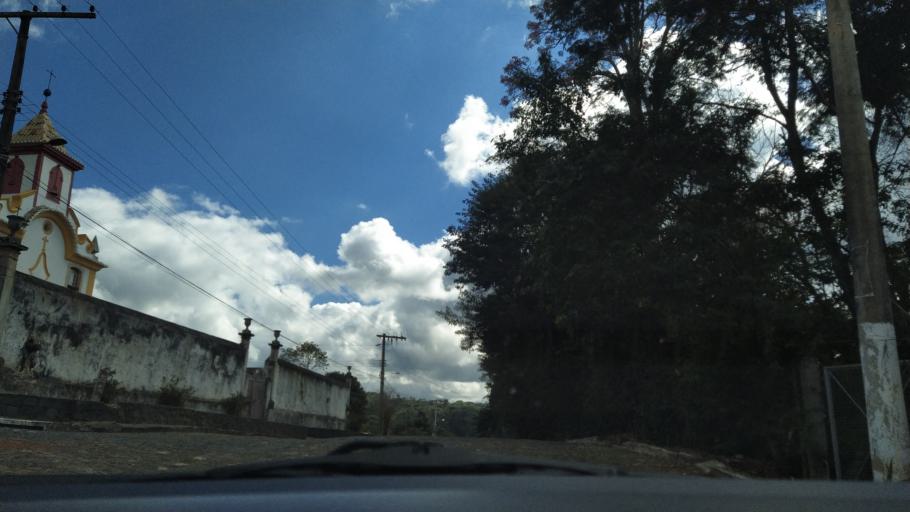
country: BR
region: Minas Gerais
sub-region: Barao De Cocais
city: Barao de Cocais
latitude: -19.8631
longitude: -43.4546
